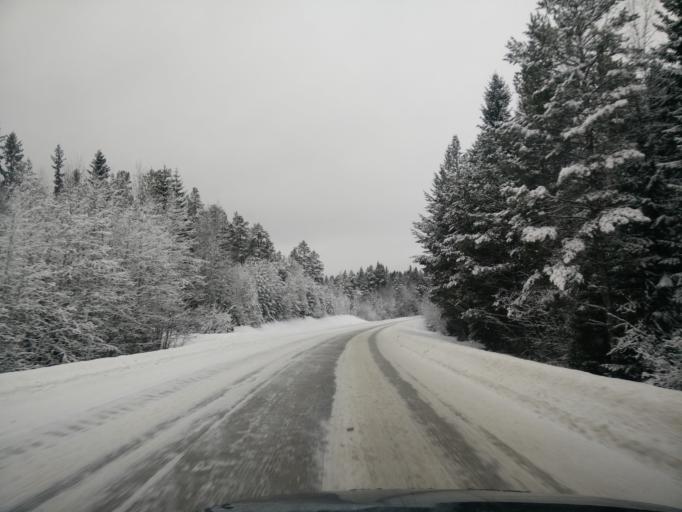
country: SE
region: Vaesternorrland
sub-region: Ange Kommun
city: Ange
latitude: 62.3923
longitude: 15.4266
